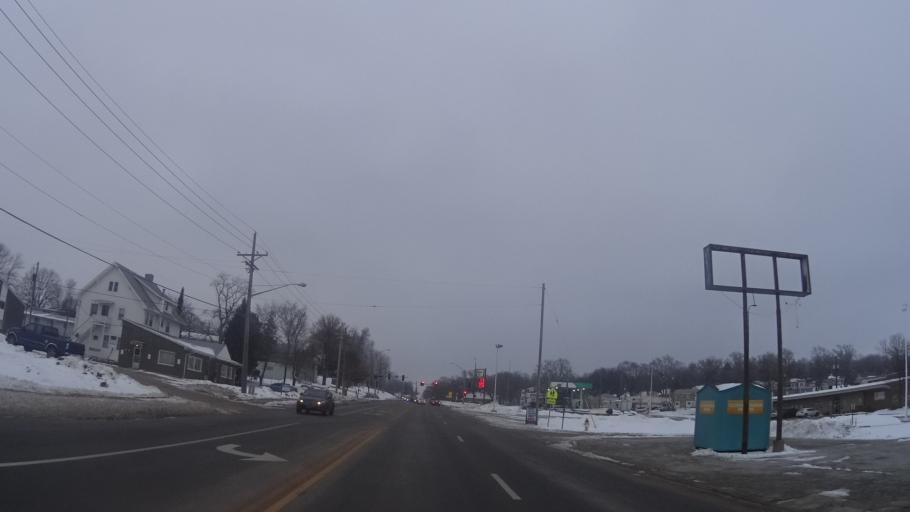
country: US
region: Nebraska
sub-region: Sarpy County
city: Bellevue
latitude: 41.1352
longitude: -95.9074
